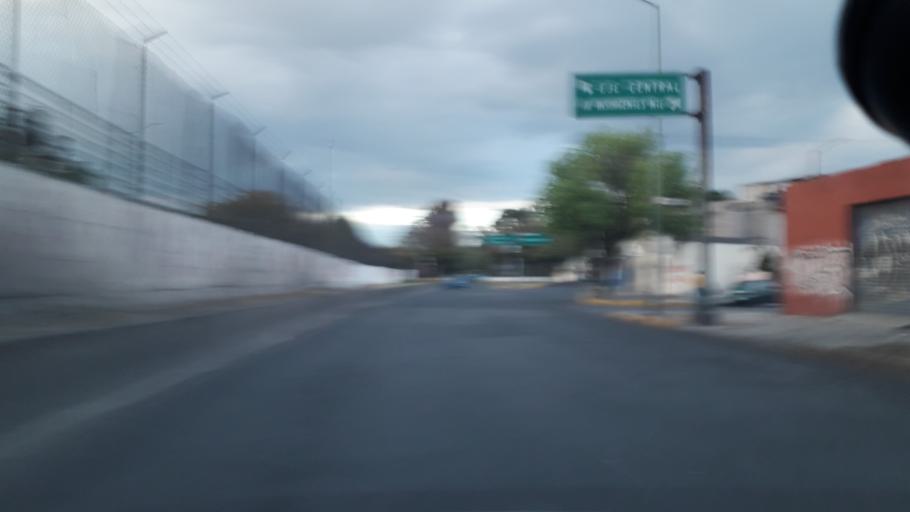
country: MX
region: Mexico City
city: Cuauhtemoc
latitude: 19.4678
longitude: -99.1352
